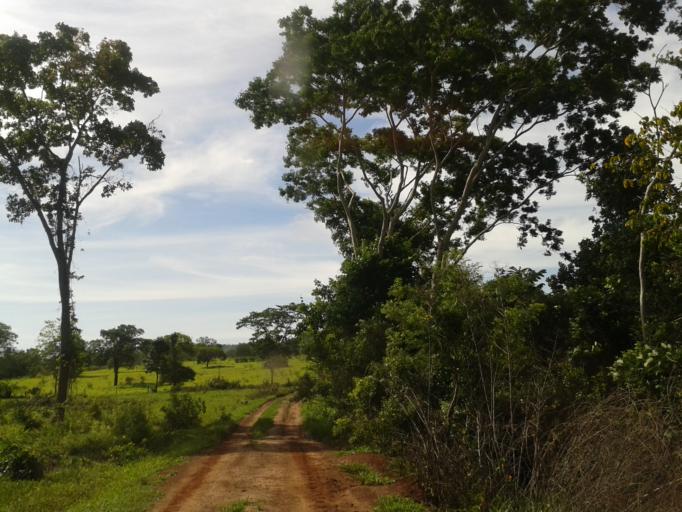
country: BR
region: Minas Gerais
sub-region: Santa Vitoria
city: Santa Vitoria
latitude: -19.0897
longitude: -50.0163
